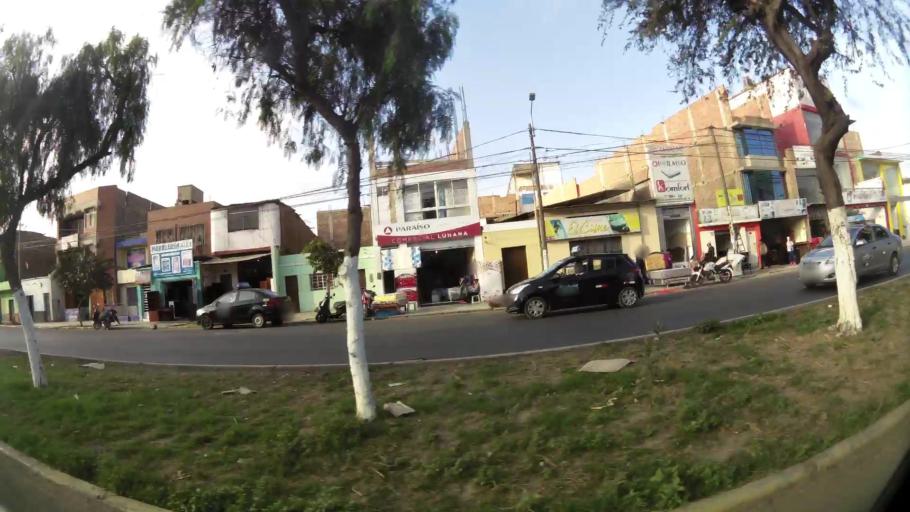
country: PE
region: La Libertad
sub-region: Provincia de Trujillo
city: El Porvenir
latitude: -8.0992
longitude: -79.0145
